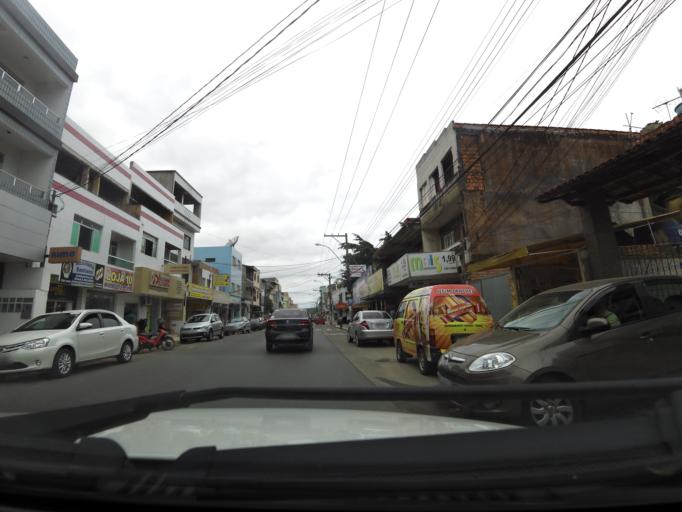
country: BR
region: Espirito Santo
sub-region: Guarapari
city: Guarapari
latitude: -20.6031
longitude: -40.4645
